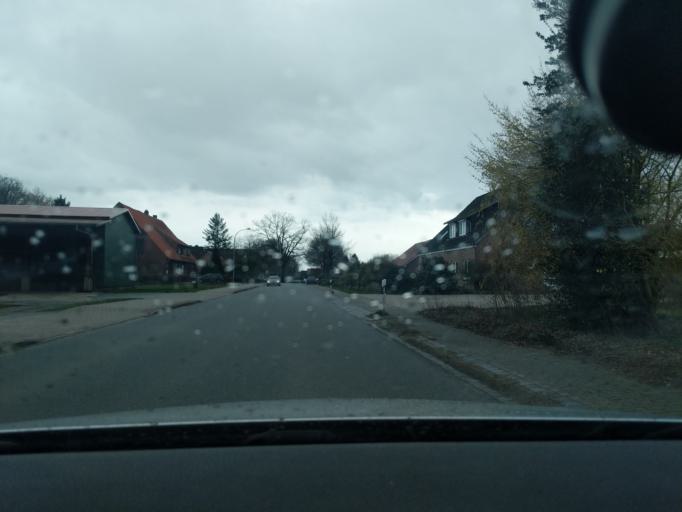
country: DE
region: Lower Saxony
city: Bargstedt
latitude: 53.4665
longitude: 9.4719
